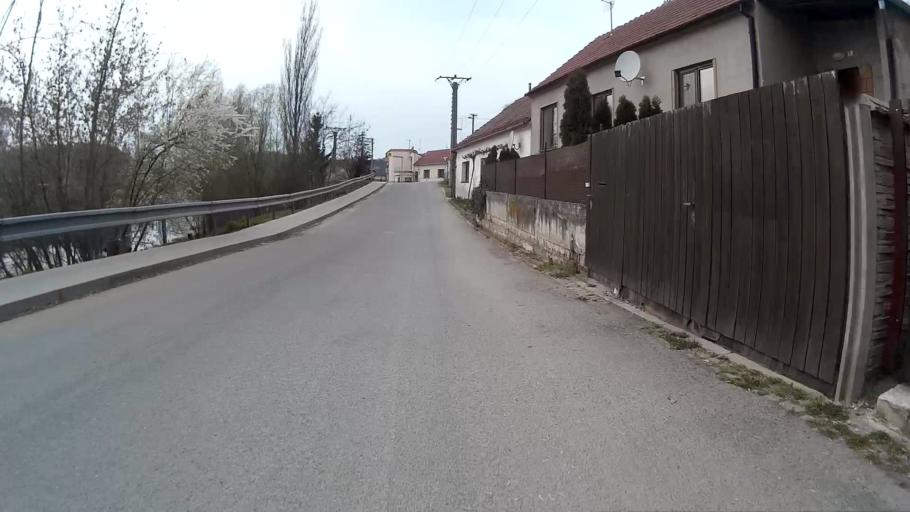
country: CZ
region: South Moravian
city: Dolni Kounice
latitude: 49.0711
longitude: 16.4710
